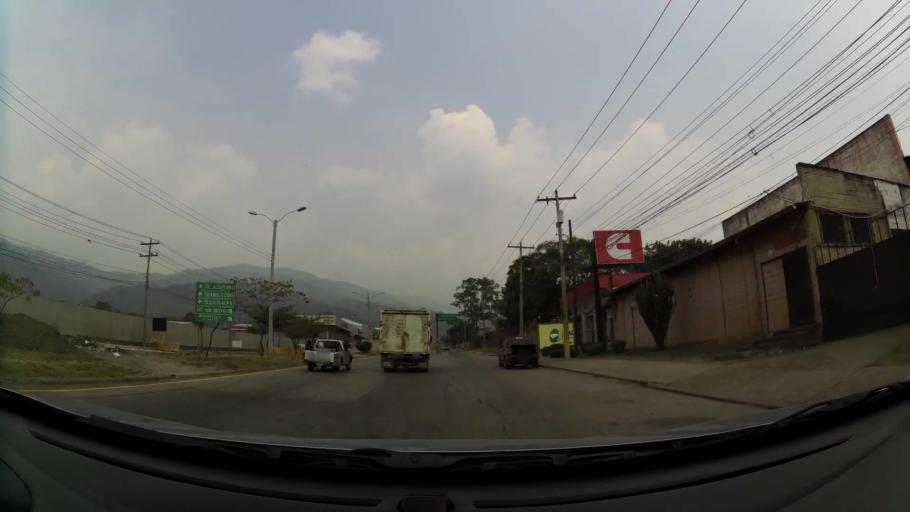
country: HN
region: Cortes
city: San Pedro Sula
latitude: 15.4768
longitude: -88.0307
